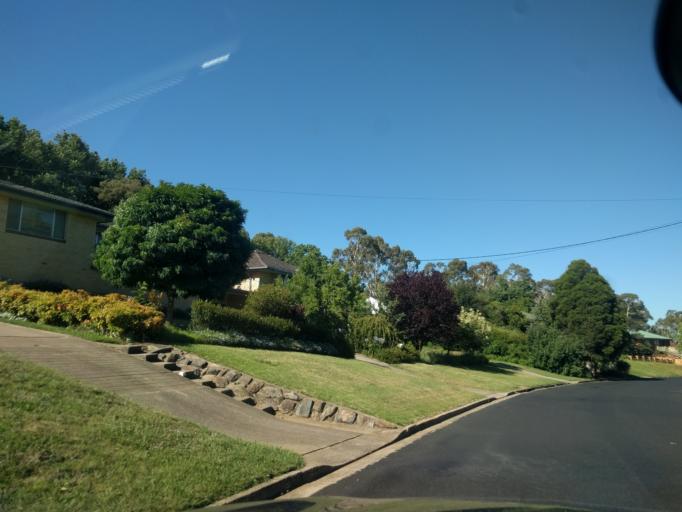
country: AU
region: New South Wales
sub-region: Armidale Dumaresq
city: Armidale
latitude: -30.5000
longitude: 151.6681
